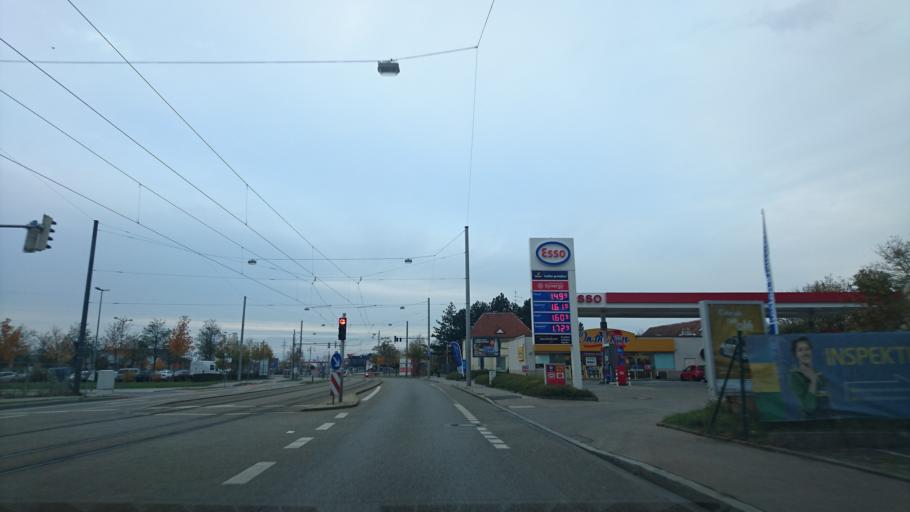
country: DE
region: Bavaria
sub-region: Swabia
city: Gersthofen
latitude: 48.4008
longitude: 10.8807
